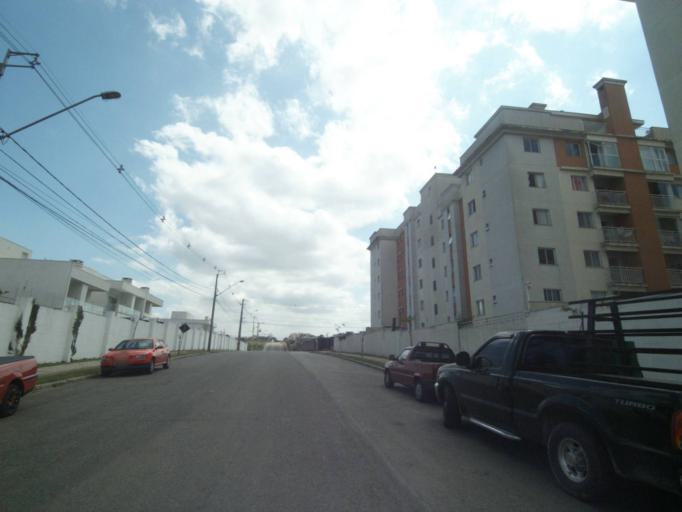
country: BR
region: Parana
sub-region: Curitiba
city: Curitiba
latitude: -25.5045
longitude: -49.3080
